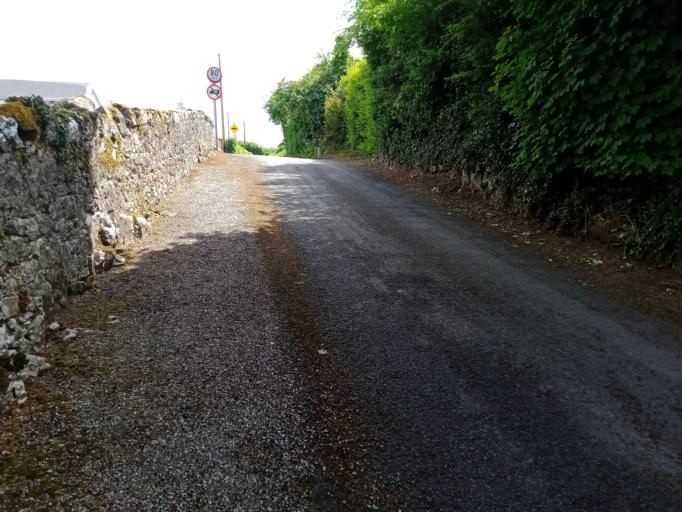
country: IE
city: Ballylinan
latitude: 52.9653
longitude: -7.0778
